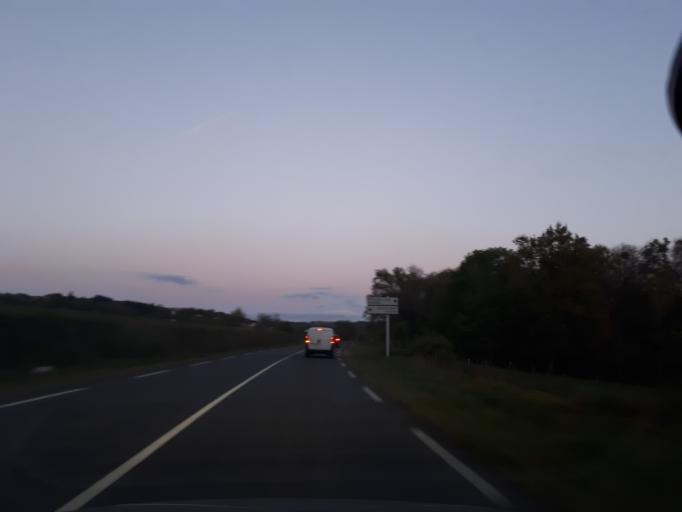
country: FR
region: Rhone-Alpes
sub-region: Departement de la Loire
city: Civens
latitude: 45.7433
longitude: 4.2755
